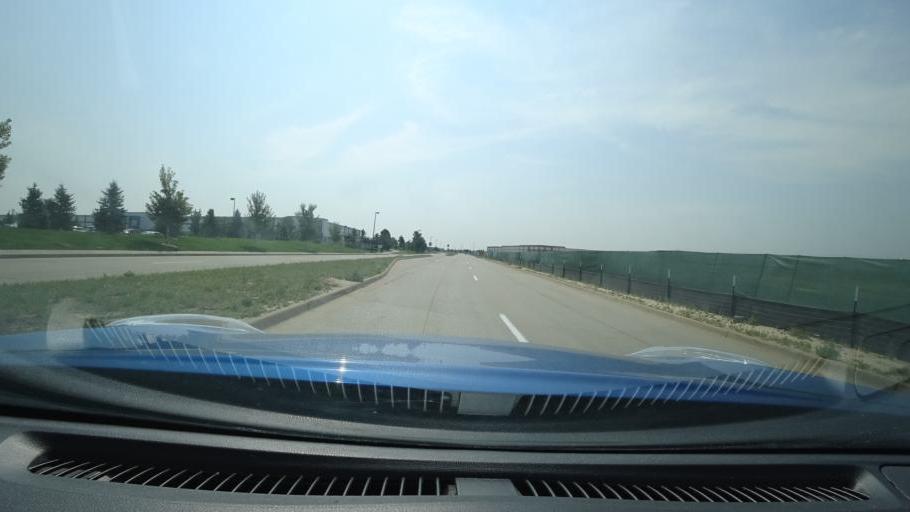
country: US
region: Colorado
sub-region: Adams County
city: Aurora
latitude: 39.7719
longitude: -104.7787
